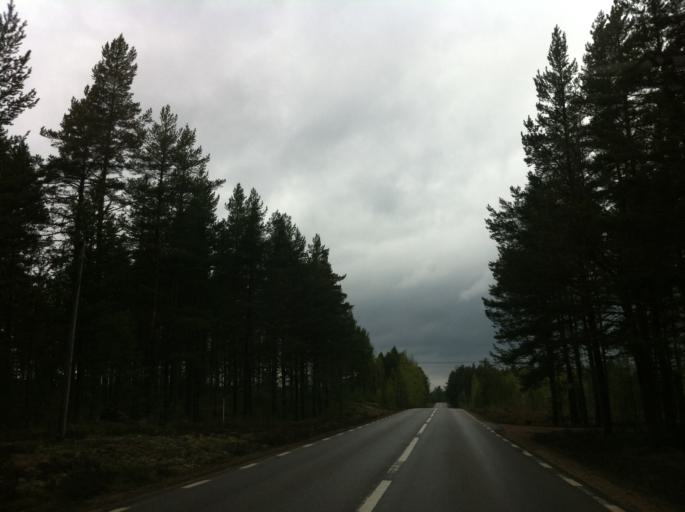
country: SE
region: Jaemtland
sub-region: Harjedalens Kommun
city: Sveg
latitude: 62.0255
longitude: 14.4402
